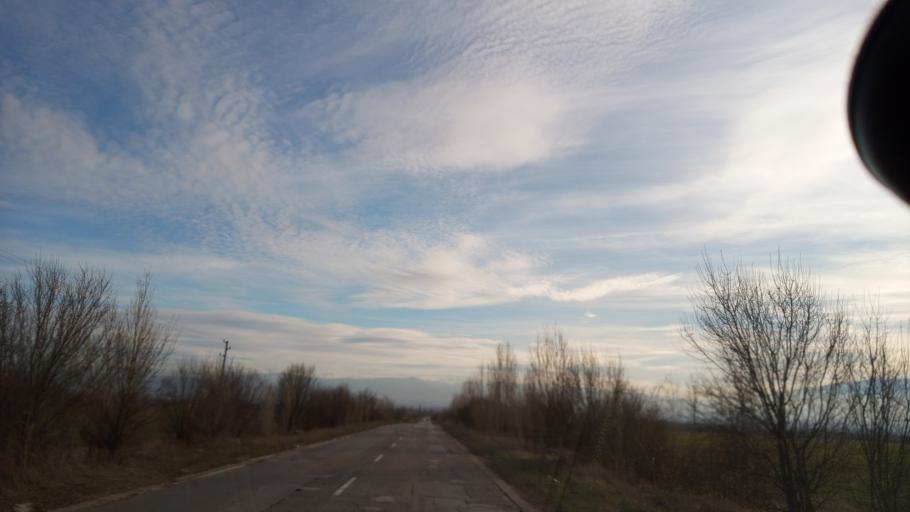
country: BG
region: Sofia-Capital
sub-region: Stolichna Obshtina
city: Bukhovo
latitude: 42.7534
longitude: 23.5581
